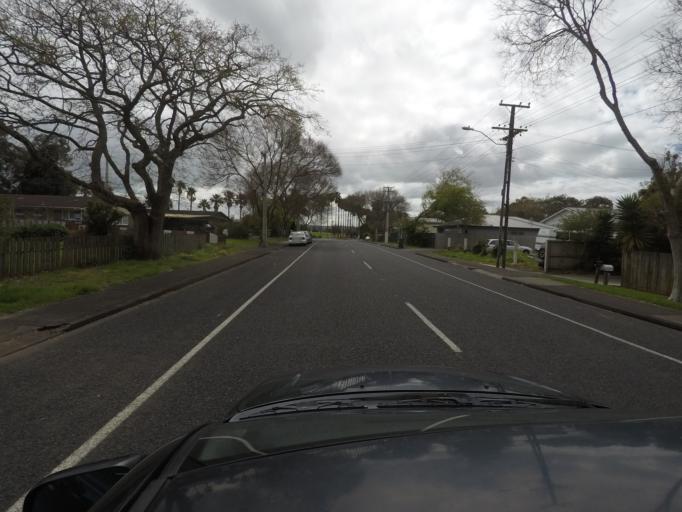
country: NZ
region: Auckland
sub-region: Auckland
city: Tamaki
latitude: -36.9353
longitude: 174.8608
